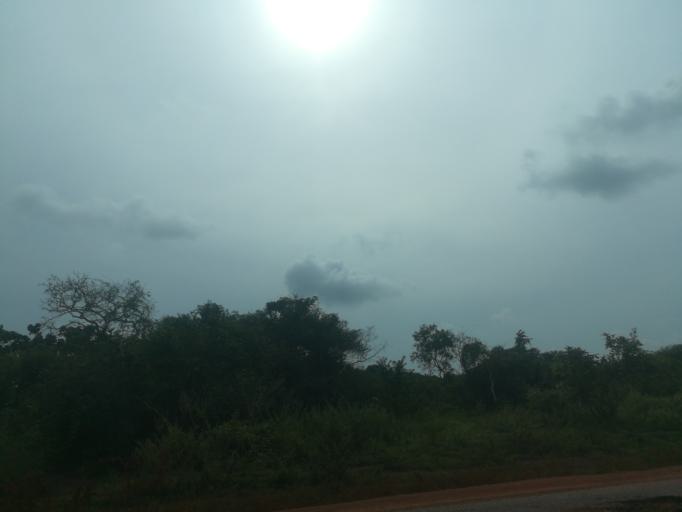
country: NG
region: Ogun
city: Ayetoro
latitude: 7.2693
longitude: 3.1047
